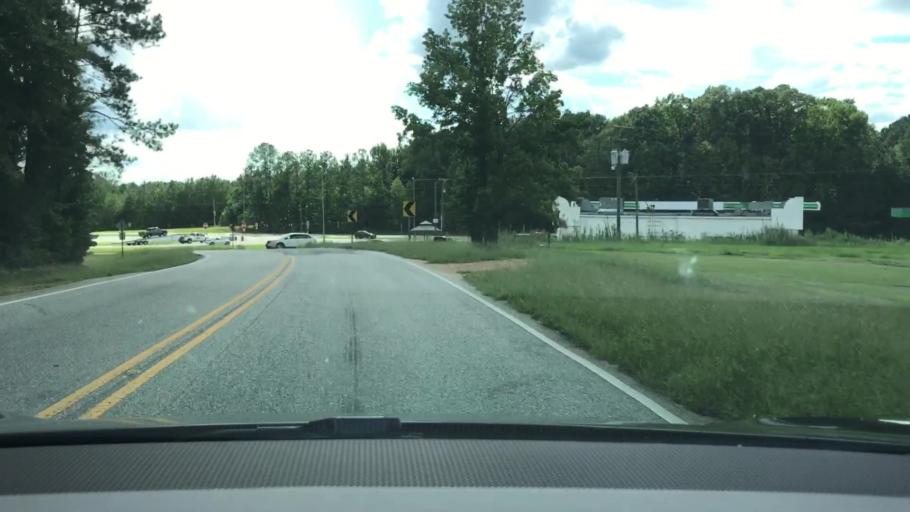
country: US
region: Alabama
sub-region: Montgomery County
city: Pike Road
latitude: 32.1933
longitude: -86.1157
